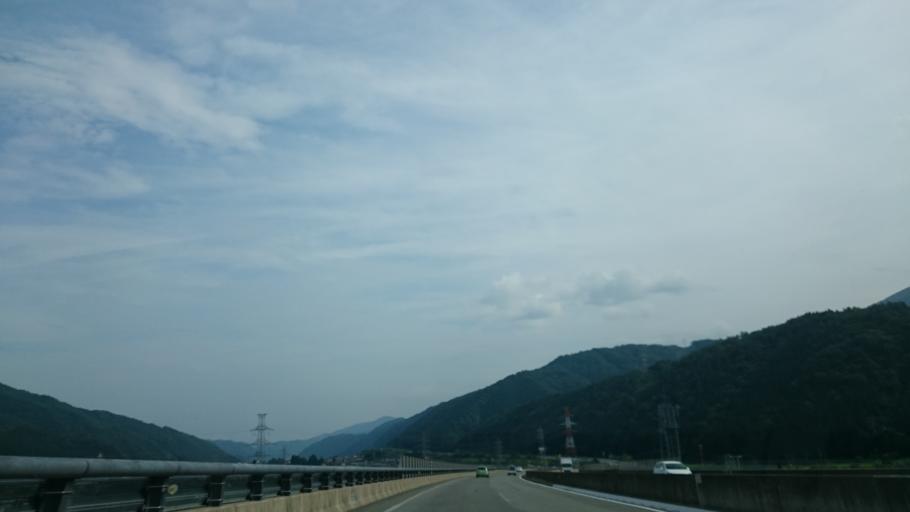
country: JP
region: Gifu
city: Gujo
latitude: 35.8542
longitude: 136.8719
